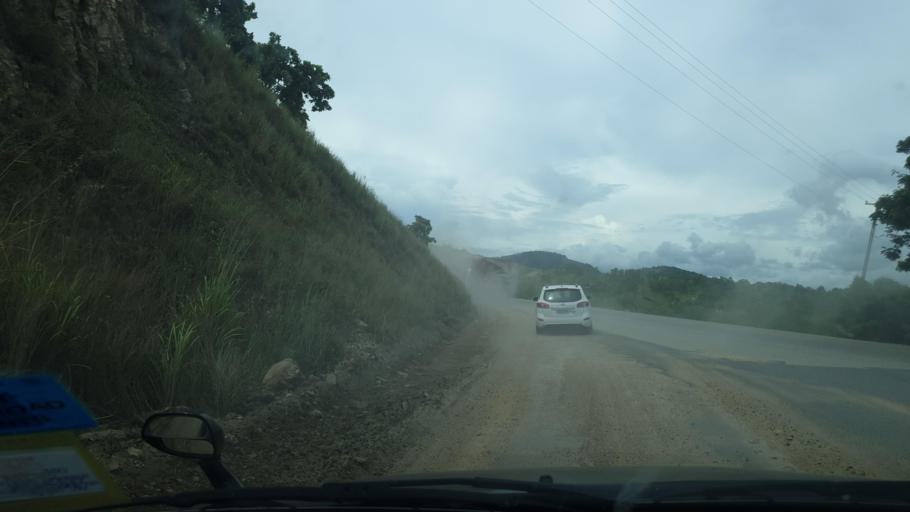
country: PG
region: National Capital
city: Port Moresby
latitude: -9.4199
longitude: 147.0992
